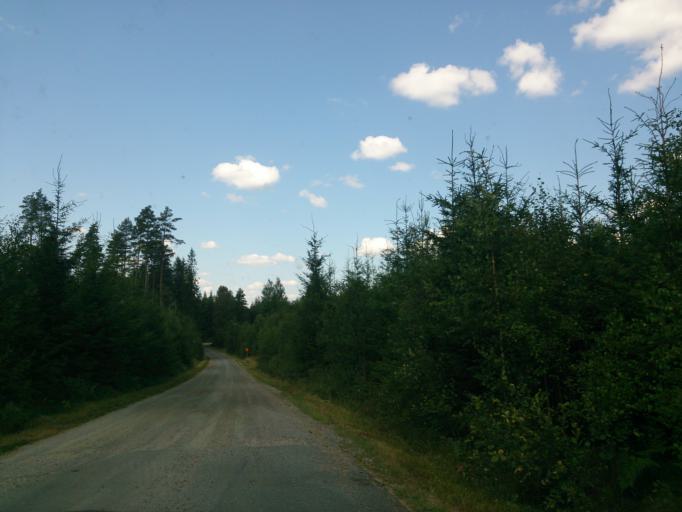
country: SE
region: Joenkoeping
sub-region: Varnamo Kommun
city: Varnamo
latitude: 57.1064
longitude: 13.9544
